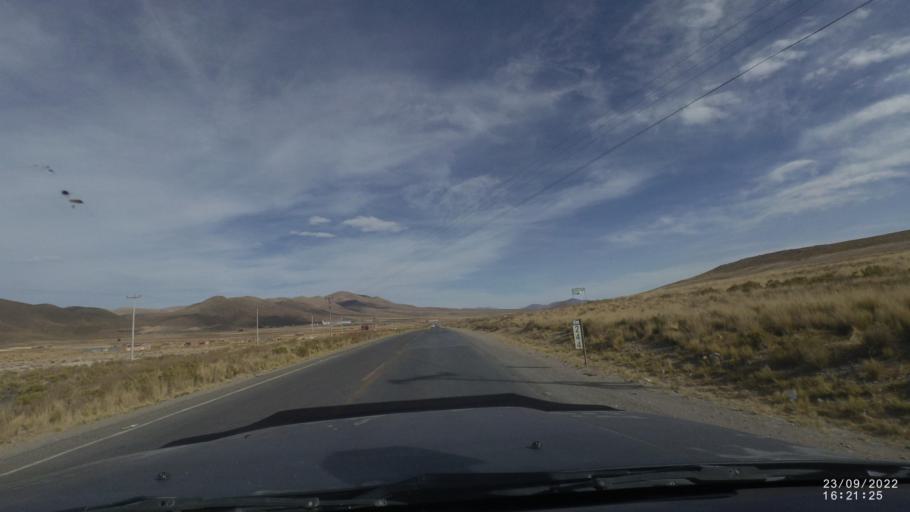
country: BO
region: Oruro
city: Machacamarca
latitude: -18.0480
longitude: -67.0116
